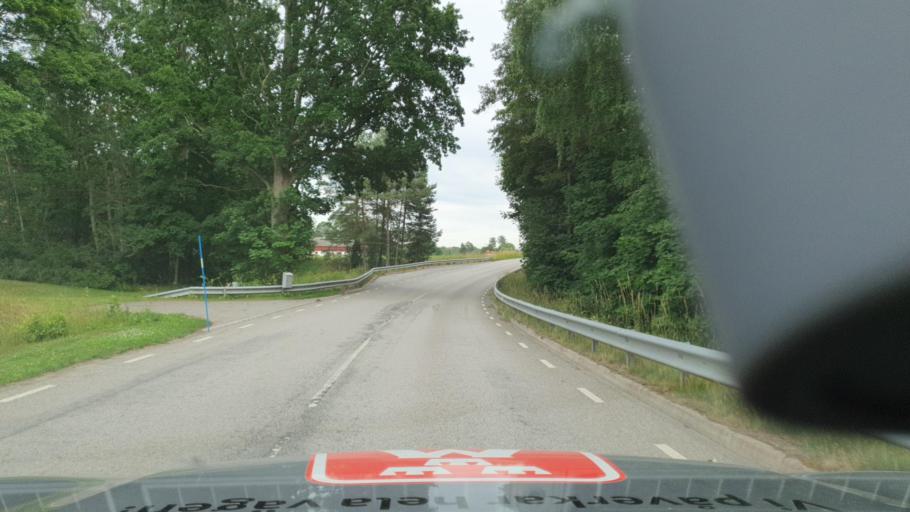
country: SE
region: Kalmar
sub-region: Nybro Kommun
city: Nybro
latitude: 56.7054
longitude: 15.9729
